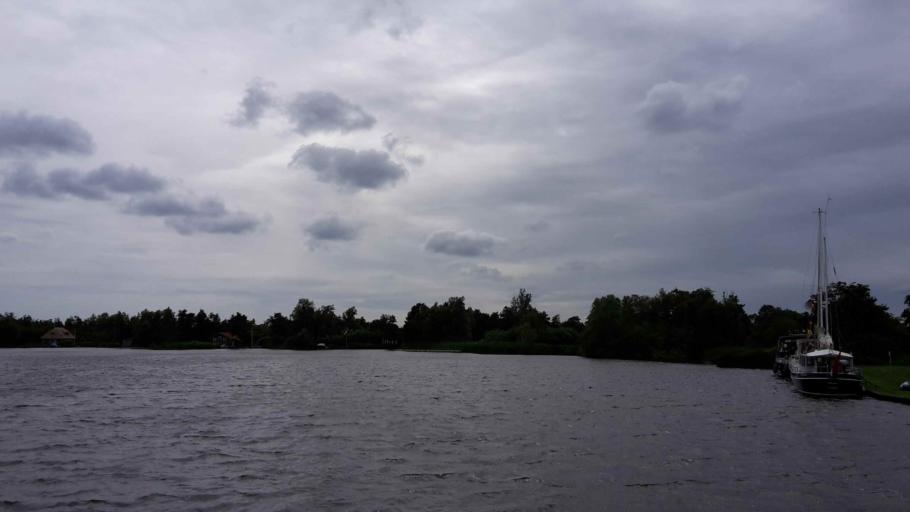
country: NL
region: Friesland
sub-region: Gemeente Boarnsterhim
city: Warten
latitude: 53.1291
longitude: 5.9228
